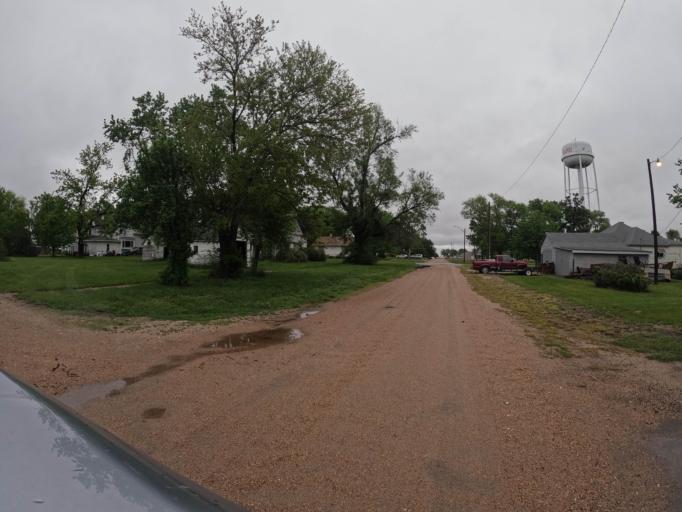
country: US
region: Nebraska
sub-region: Clay County
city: Harvard
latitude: 40.6244
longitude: -98.0965
